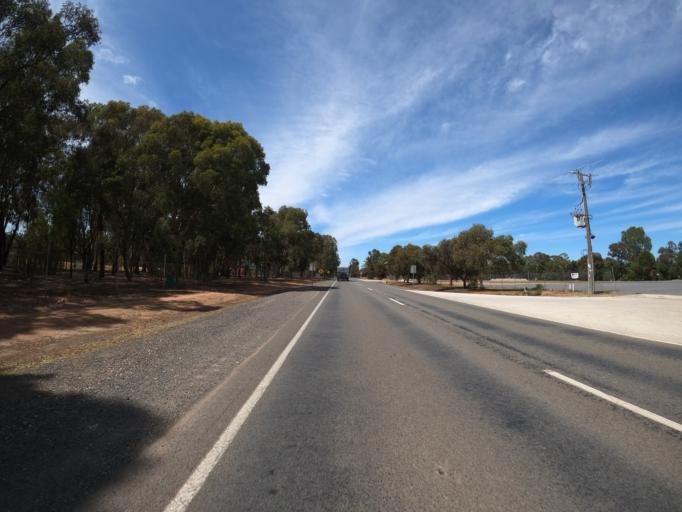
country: AU
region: Victoria
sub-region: Moira
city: Yarrawonga
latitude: -36.0346
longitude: 145.9955
